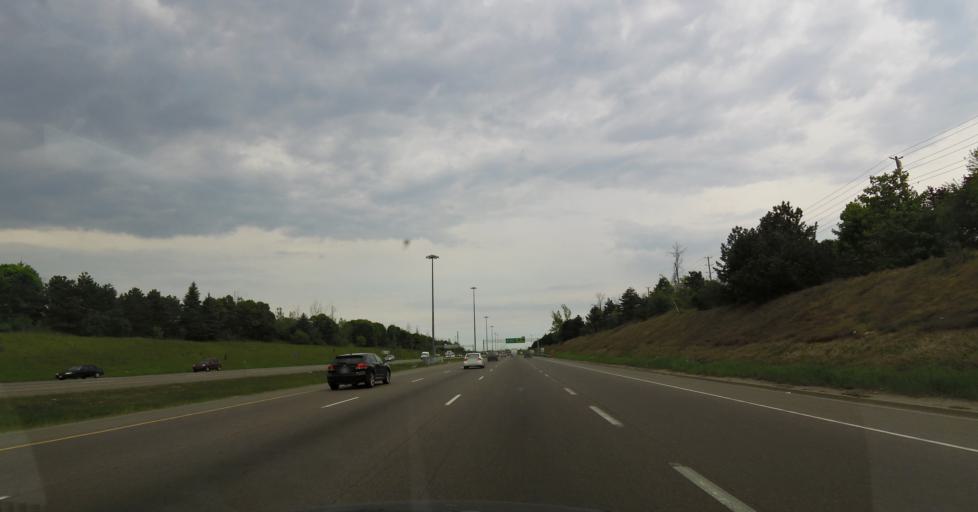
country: CA
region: Ontario
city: Brampton
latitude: 43.7120
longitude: -79.7475
